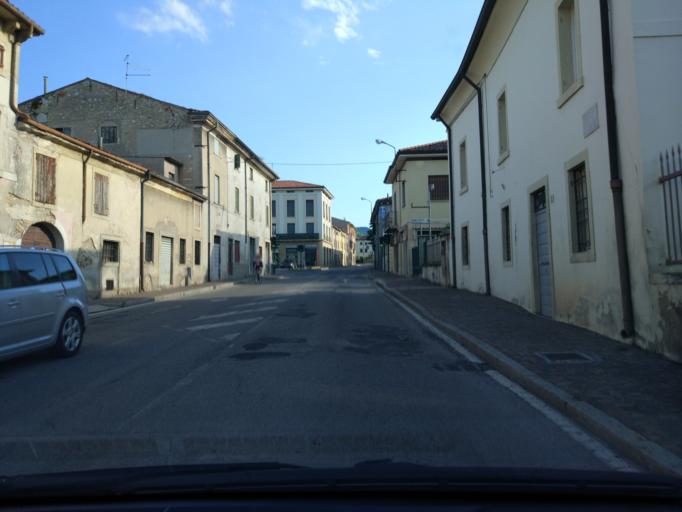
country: IT
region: Veneto
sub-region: Provincia di Verona
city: Illasi
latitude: 45.4661
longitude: 11.1797
